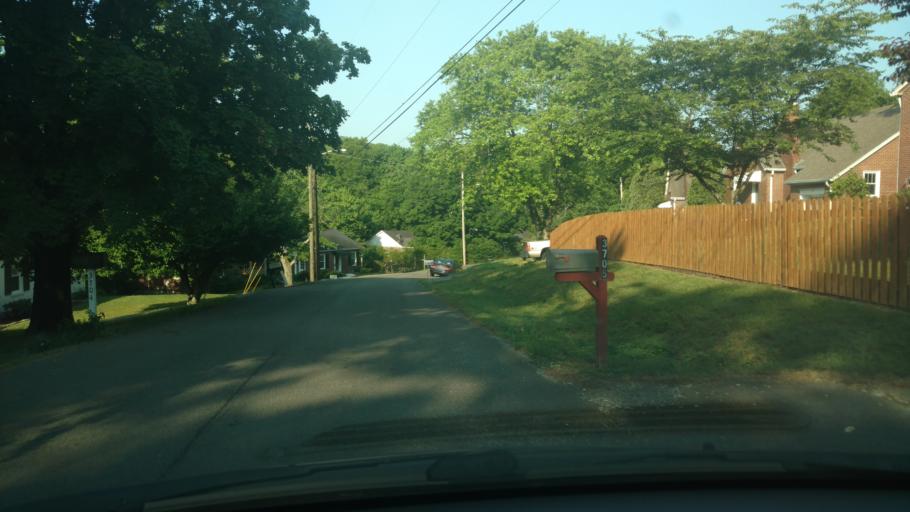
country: US
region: Tennessee
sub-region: Davidson County
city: Nashville
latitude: 36.2086
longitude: -86.7182
